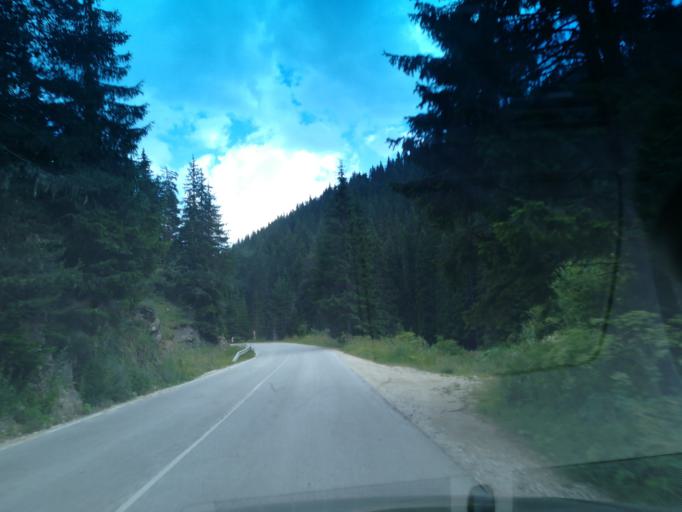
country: BG
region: Smolyan
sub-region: Obshtina Chepelare
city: Chepelare
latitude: 41.6632
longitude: 24.6606
